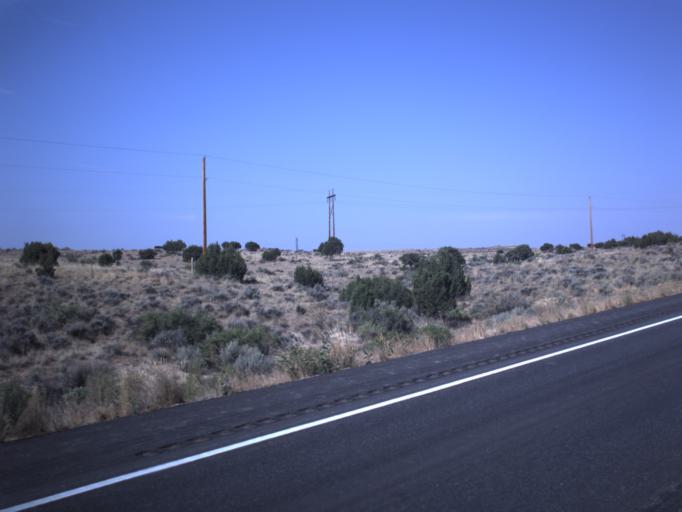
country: US
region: Utah
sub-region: Uintah County
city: Naples
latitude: 40.3206
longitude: -109.2550
